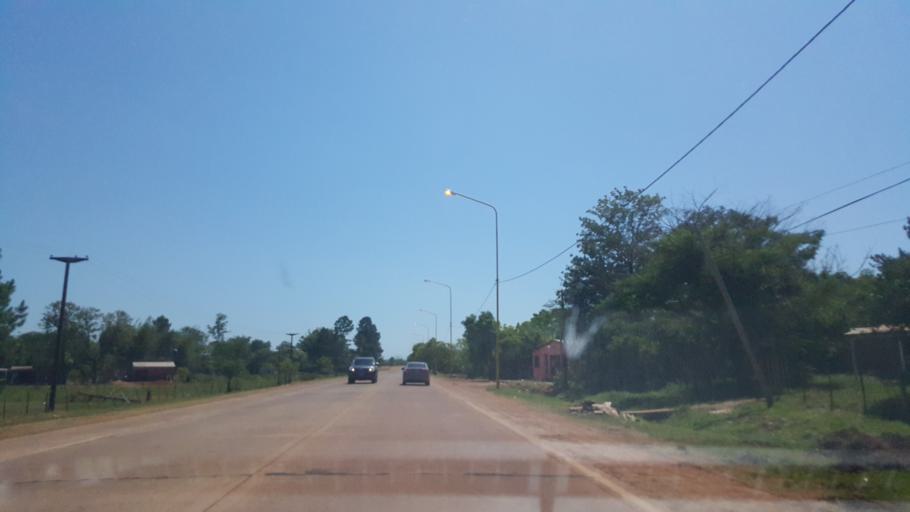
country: AR
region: Corrientes
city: Santo Tome
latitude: -28.5504
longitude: -56.0661
